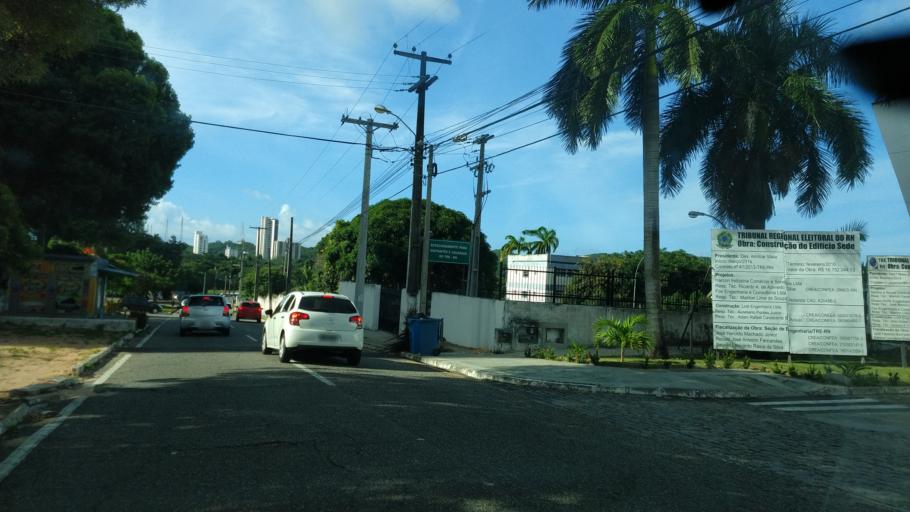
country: BR
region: Rio Grande do Norte
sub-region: Natal
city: Natal
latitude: -5.8099
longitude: -35.2008
